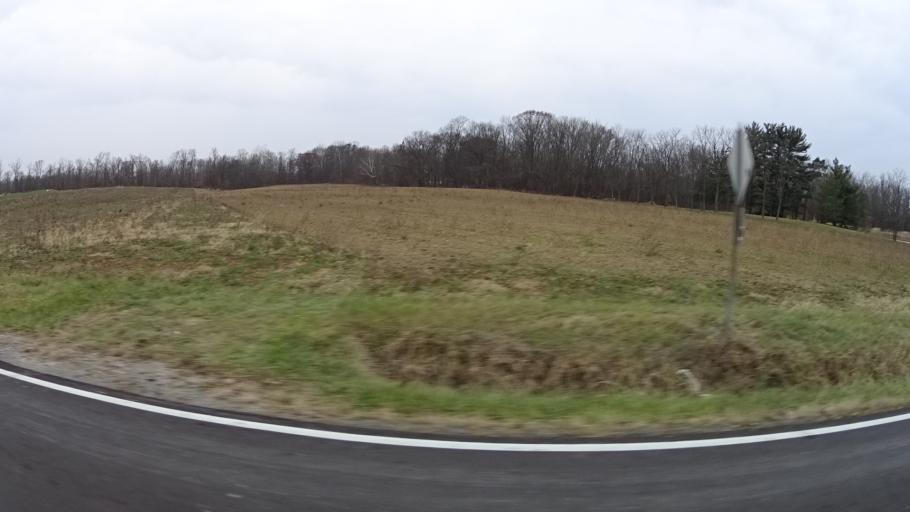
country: US
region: Ohio
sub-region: Lorain County
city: Lagrange
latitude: 41.2005
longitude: -82.0792
